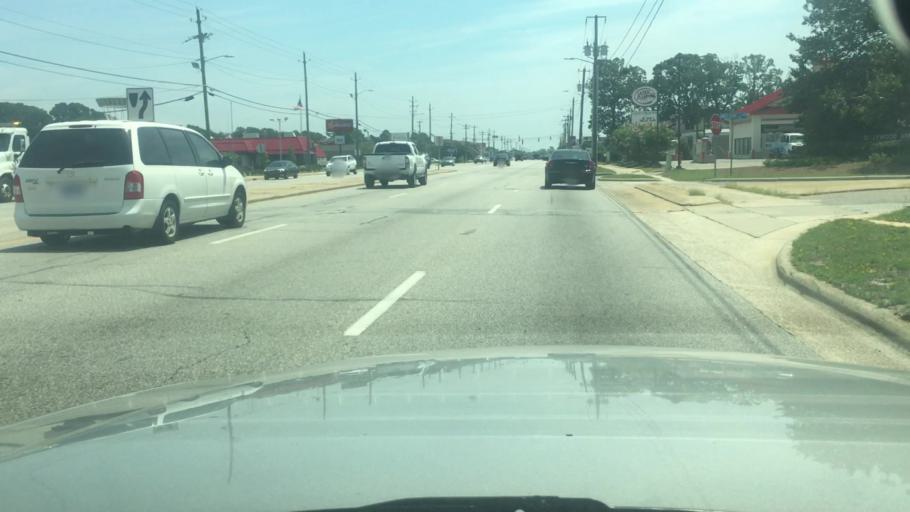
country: US
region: North Carolina
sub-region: Cumberland County
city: Fayetteville
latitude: 35.0445
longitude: -78.9331
